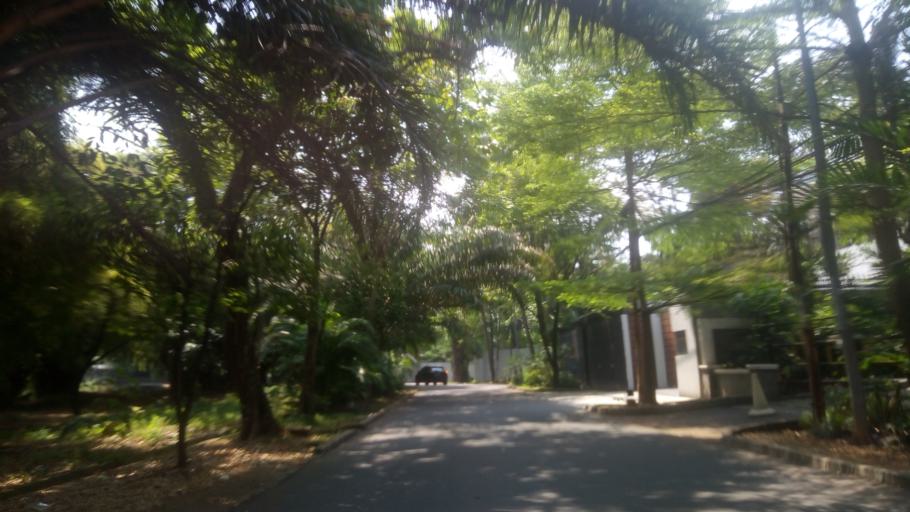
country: ID
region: Jakarta Raya
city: Jakarta
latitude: -6.2377
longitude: 106.8357
